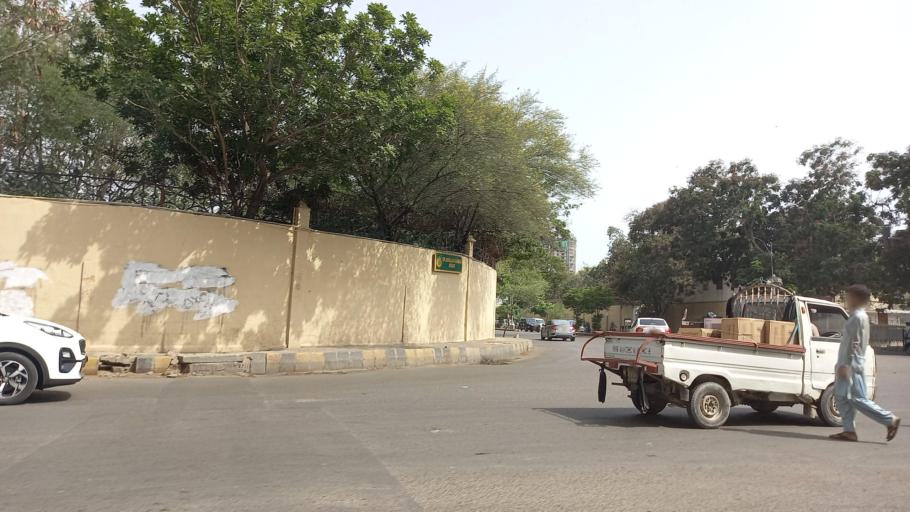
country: PK
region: Sindh
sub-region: Karachi District
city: Karachi
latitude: 24.8499
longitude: 67.0306
